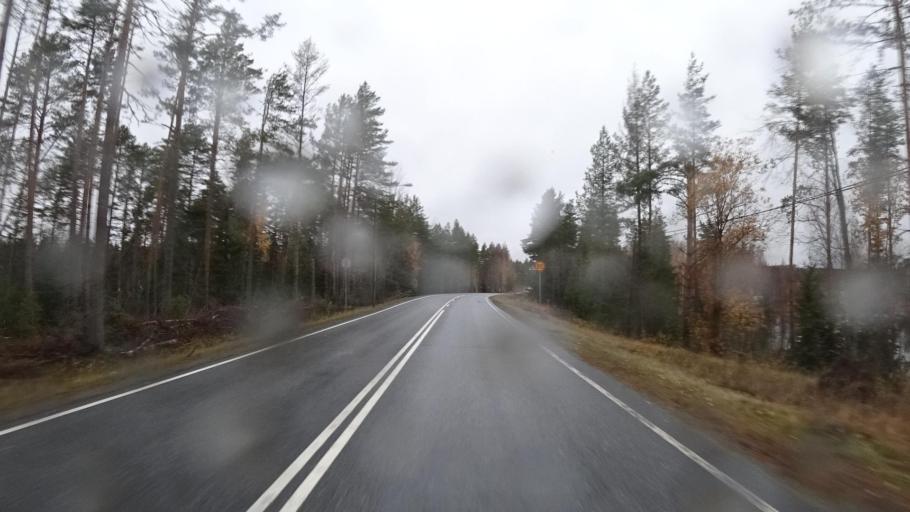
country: FI
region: Northern Savo
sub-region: Koillis-Savo
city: Juankoski
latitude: 62.8770
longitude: 28.2941
